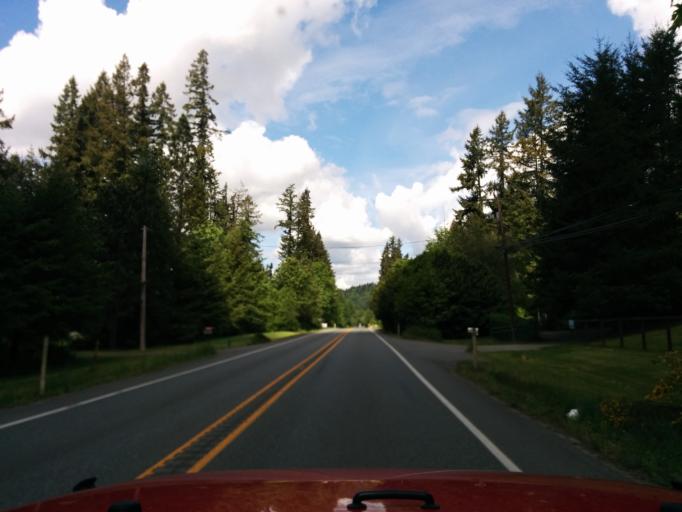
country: US
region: Washington
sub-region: King County
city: Union Hill-Novelty Hill
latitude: 47.6483
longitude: -122.0426
